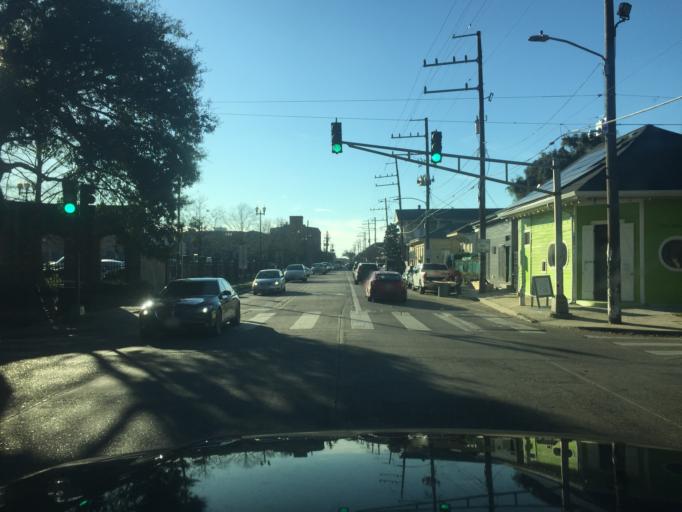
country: US
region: Louisiana
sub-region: Jefferson Parish
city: Marrero
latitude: 29.9172
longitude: -90.1011
